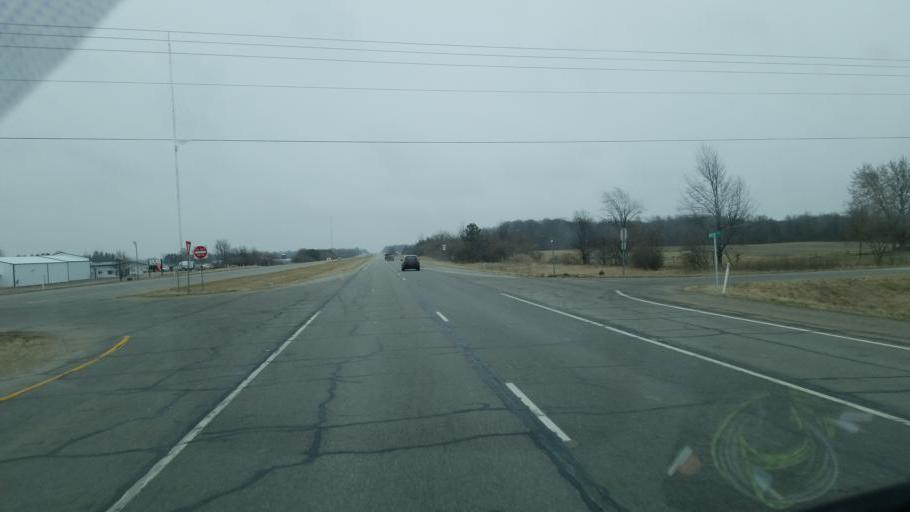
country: US
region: Indiana
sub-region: Wabash County
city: Wabash
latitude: 40.8079
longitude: -85.9424
